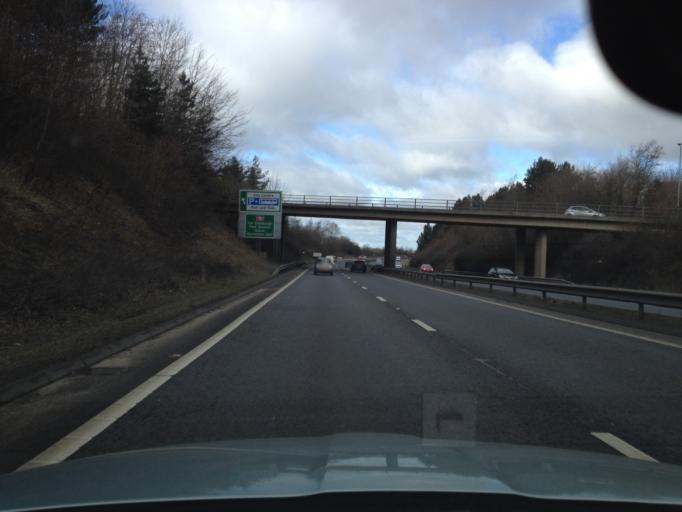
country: GB
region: Scotland
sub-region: Edinburgh
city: Currie
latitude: 55.9134
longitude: -3.2913
